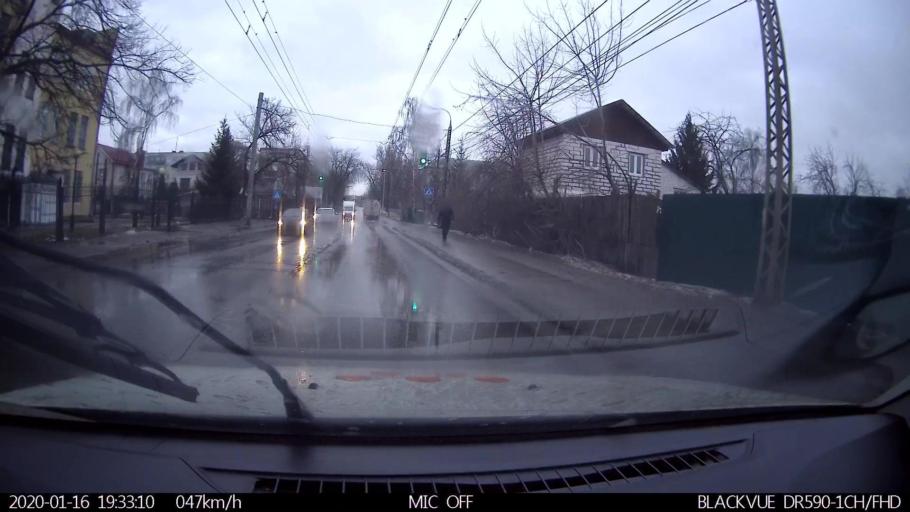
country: RU
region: Nizjnij Novgorod
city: Neklyudovo
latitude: 56.3619
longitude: 43.8451
